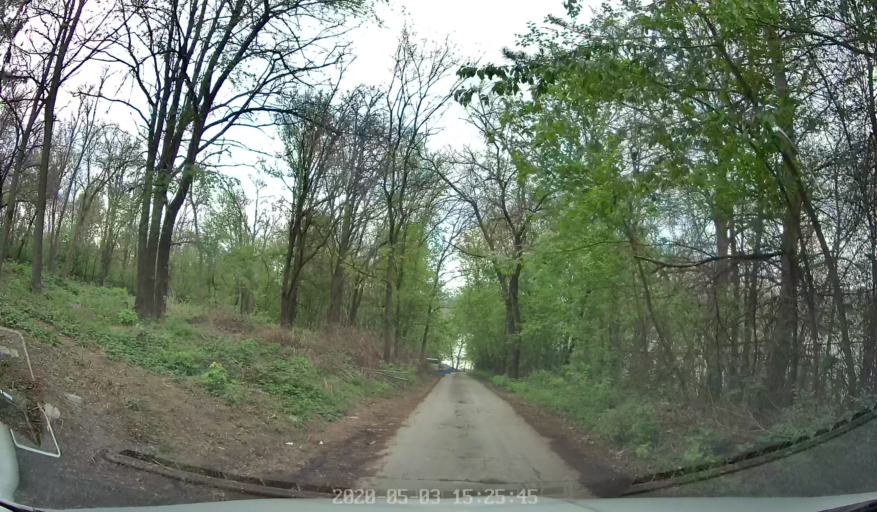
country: MD
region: Chisinau
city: Vatra
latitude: 47.0914
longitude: 28.7111
